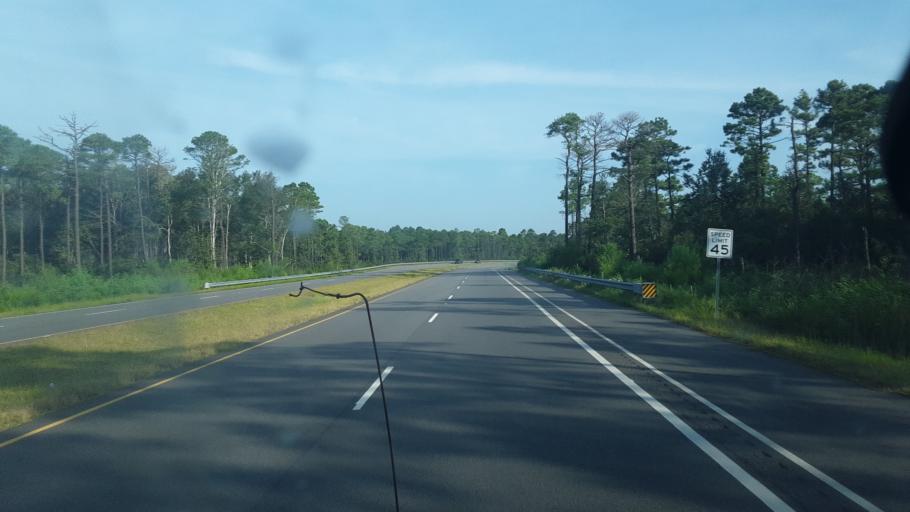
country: US
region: South Carolina
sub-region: Horry County
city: Myrtle Beach
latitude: 33.7912
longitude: -78.8811
